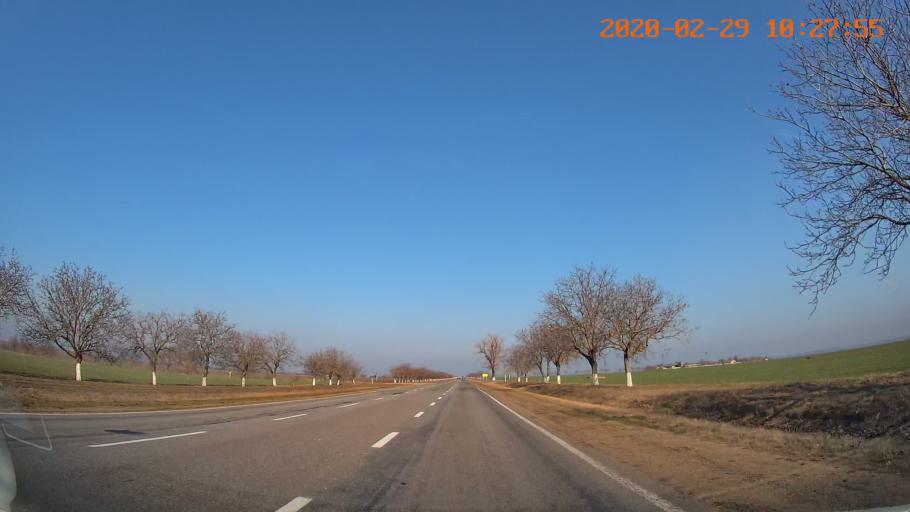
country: MD
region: Telenesti
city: Tiraspolul Nou
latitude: 46.9029
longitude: 29.5948
